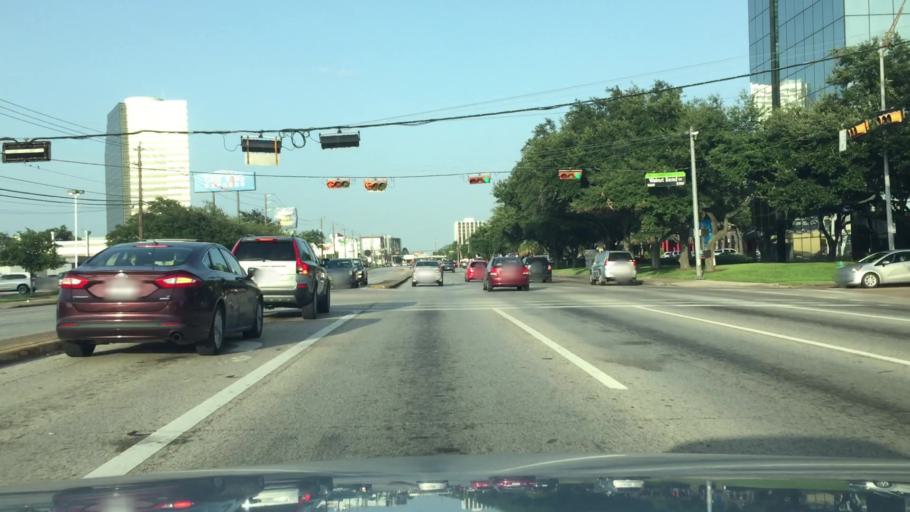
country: US
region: Texas
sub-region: Harris County
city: Bunker Hill Village
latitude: 29.7368
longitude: -95.5672
